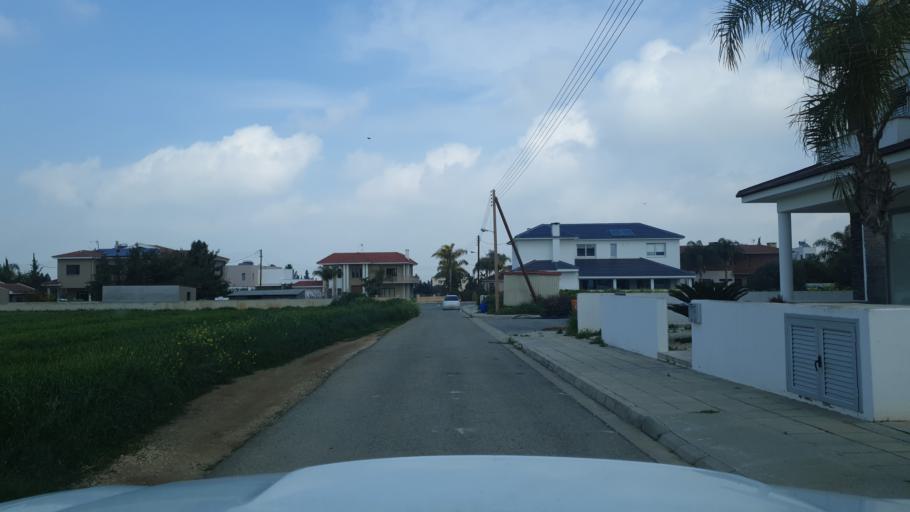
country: CY
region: Lefkosia
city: Kato Deftera
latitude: 35.0856
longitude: 33.2887
